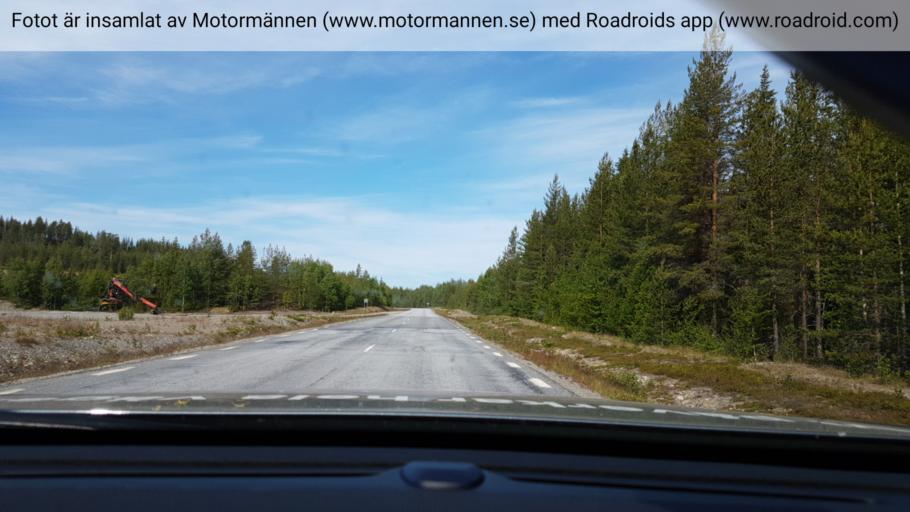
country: SE
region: Vaesterbotten
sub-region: Asele Kommun
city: Asele
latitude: 64.2070
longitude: 16.9858
